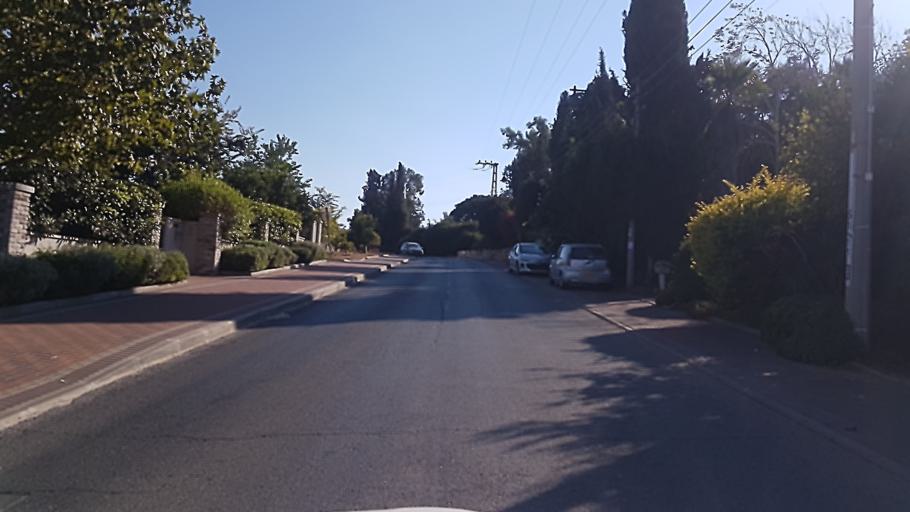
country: IL
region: Central District
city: Kfar Saba
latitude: 32.2080
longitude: 34.9041
